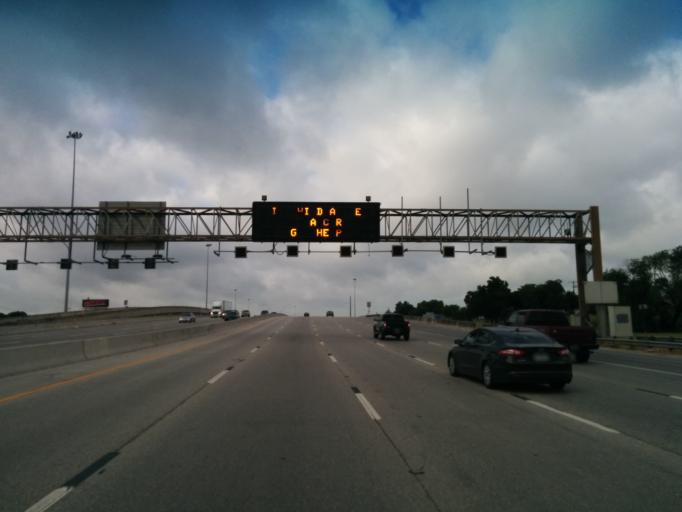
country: US
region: Texas
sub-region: Bexar County
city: Olmos Park
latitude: 29.4637
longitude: -98.5160
